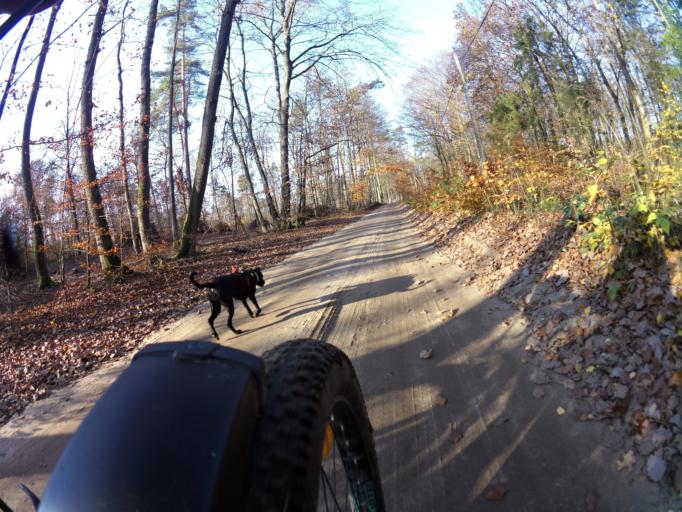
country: PL
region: Pomeranian Voivodeship
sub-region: Powiat pucki
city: Krokowa
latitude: 54.7276
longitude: 18.2080
